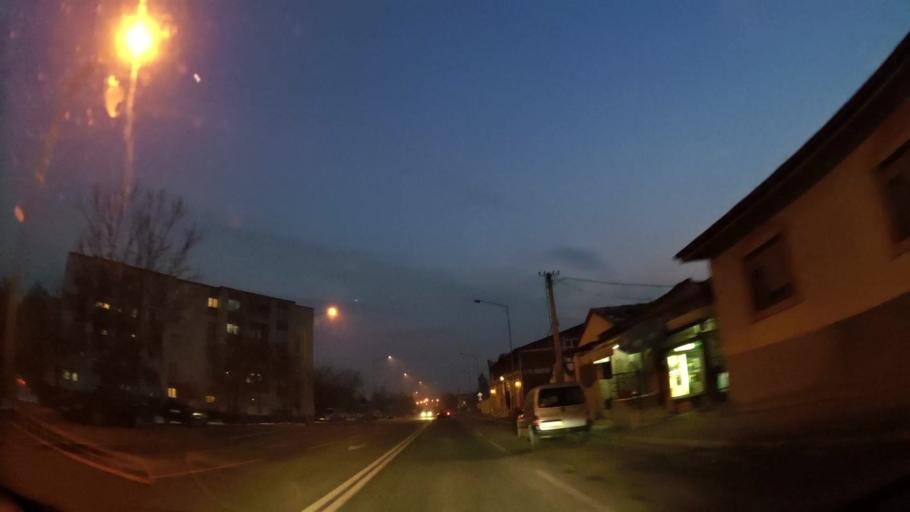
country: MK
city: Creshevo
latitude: 42.0026
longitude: 21.5032
